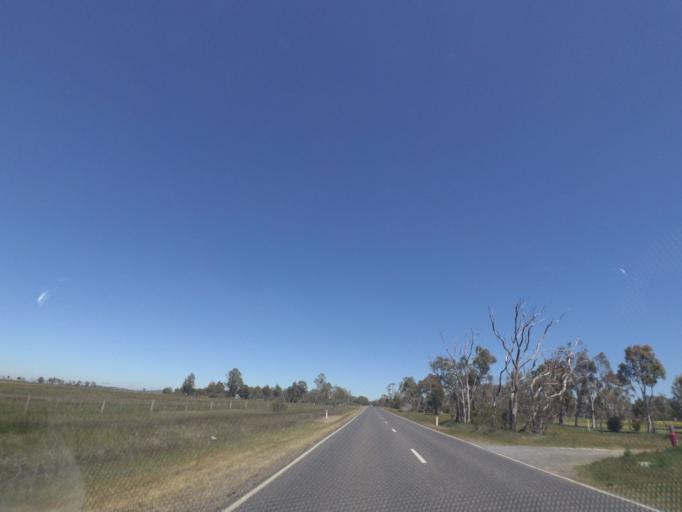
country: AU
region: Victoria
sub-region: Hume
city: Craigieburn
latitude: -37.2921
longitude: 144.8829
